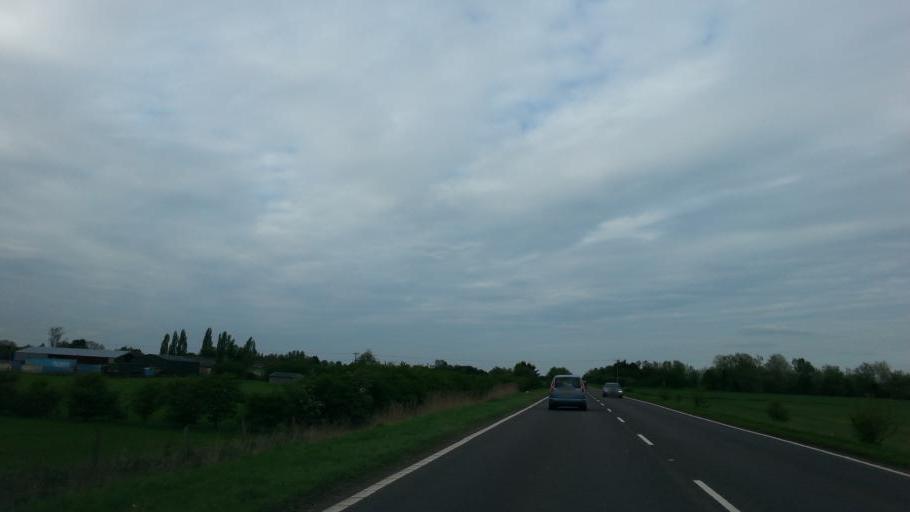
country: GB
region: England
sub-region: Cambridgeshire
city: Doddington
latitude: 52.4875
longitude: 0.0659
